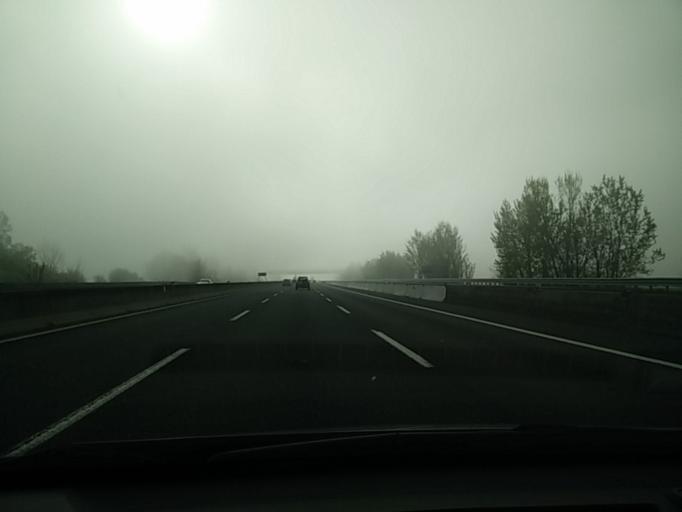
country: IT
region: Emilia-Romagna
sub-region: Provincia di Bologna
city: Ozzano dell'Emilia
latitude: 44.4726
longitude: 11.4696
